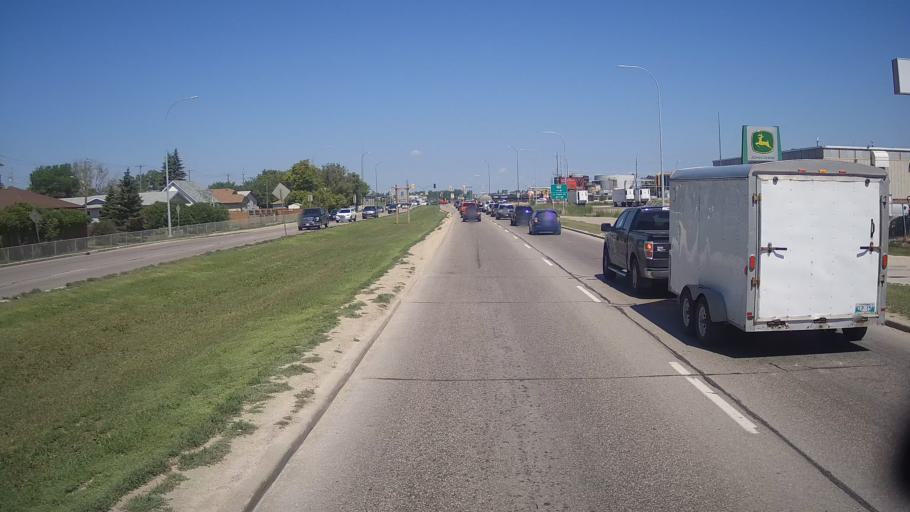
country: CA
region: Manitoba
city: Winnipeg
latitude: 49.8836
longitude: -97.0721
